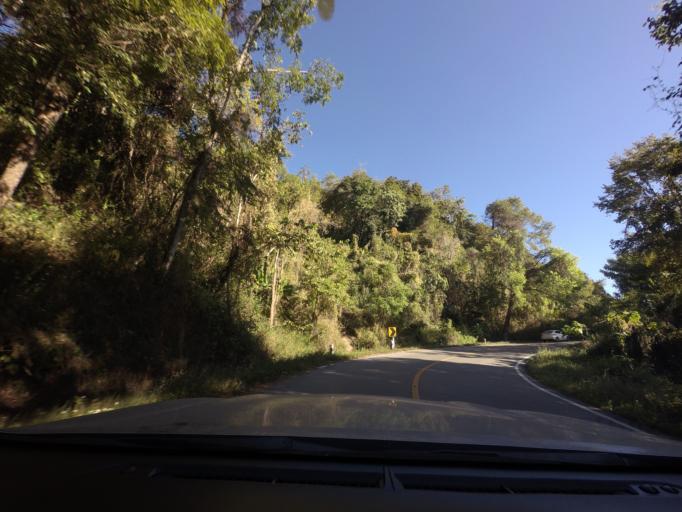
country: TH
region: Mae Hong Son
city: Mae Hi
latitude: 19.2254
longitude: 98.6719
